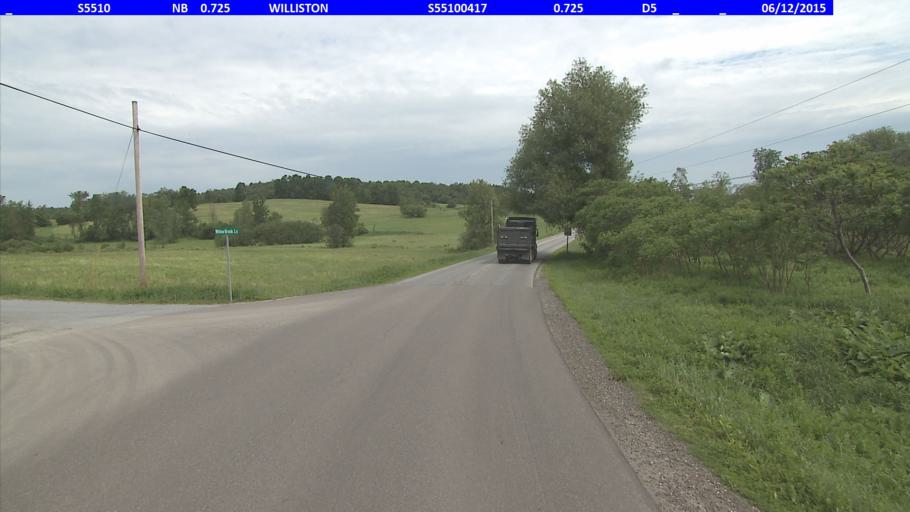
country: US
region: Vermont
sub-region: Chittenden County
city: Hinesburg
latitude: 44.3828
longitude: -73.0977
